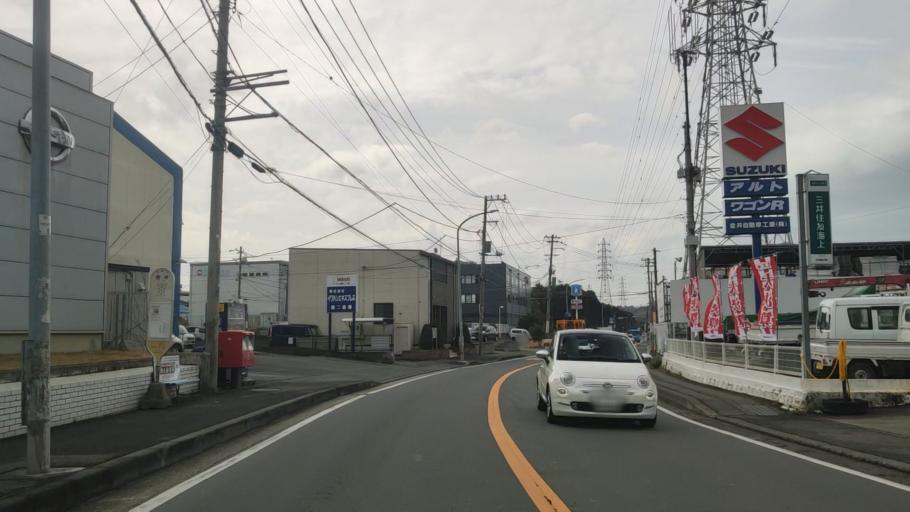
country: JP
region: Kanagawa
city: Fujisawa
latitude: 35.3783
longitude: 139.5257
